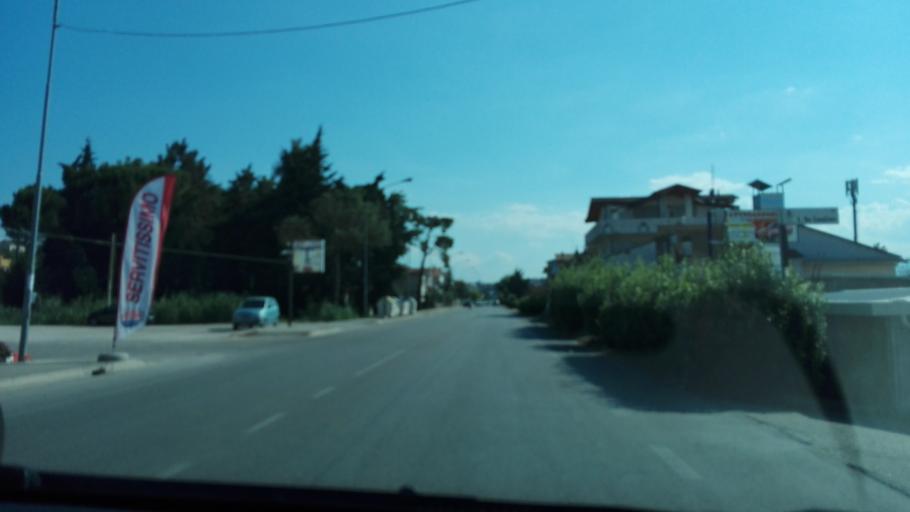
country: IT
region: Abruzzo
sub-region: Provincia di Pescara
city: Cappelle sul Tavo
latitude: 42.4882
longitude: 14.1206
